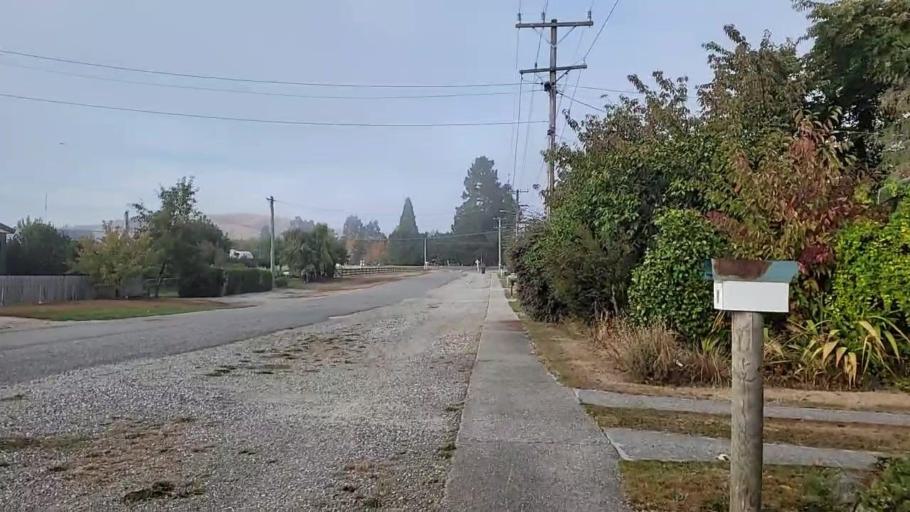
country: NZ
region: Southland
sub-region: Gore District
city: Gore
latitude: -45.6311
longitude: 169.3616
